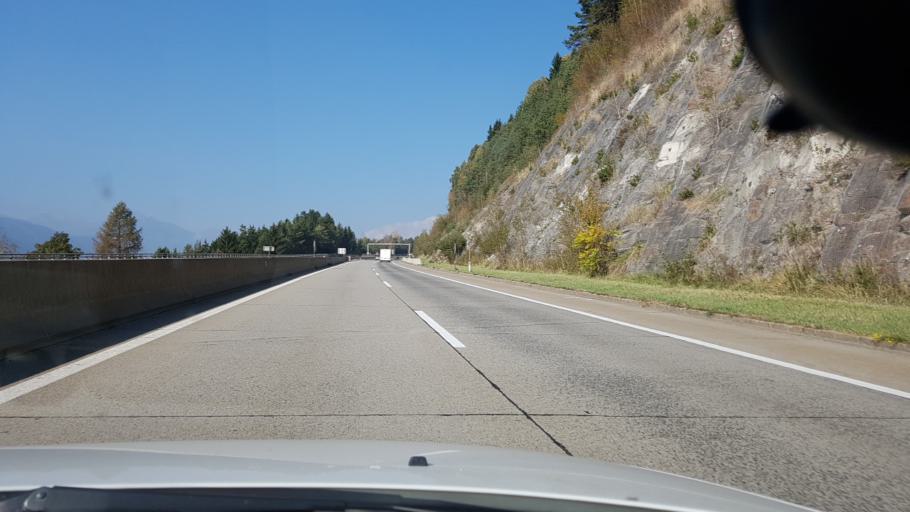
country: AT
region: Carinthia
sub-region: Politischer Bezirk Spittal an der Drau
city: Spittal an der Drau
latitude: 46.7892
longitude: 13.5252
